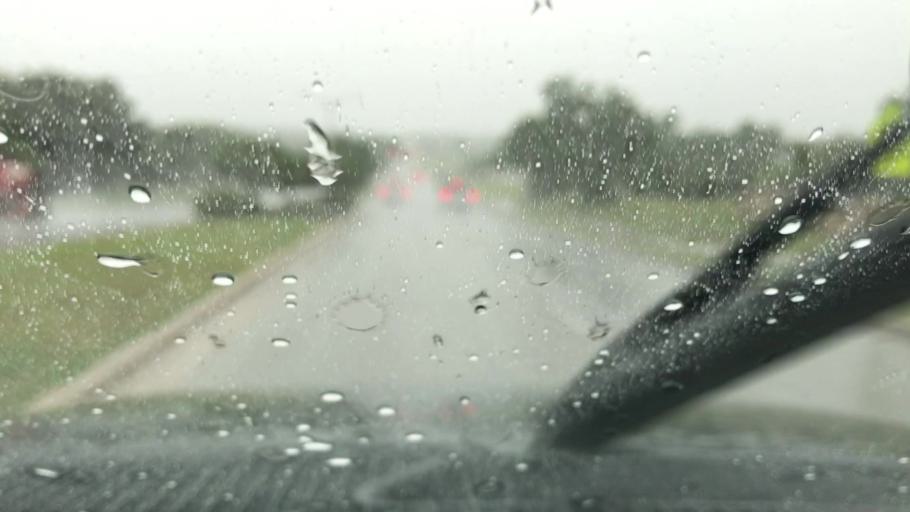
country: US
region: Texas
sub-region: Williamson County
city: Leander
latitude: 30.5402
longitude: -97.8626
